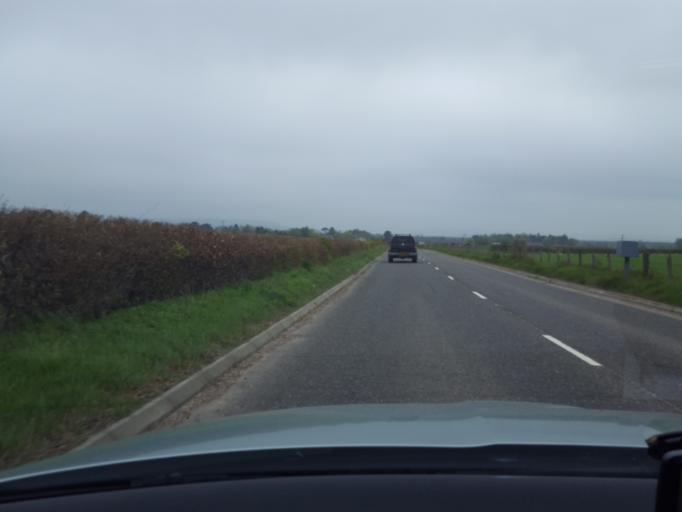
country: GB
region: Scotland
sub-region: Angus
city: Brechin
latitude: 56.7749
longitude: -2.6440
